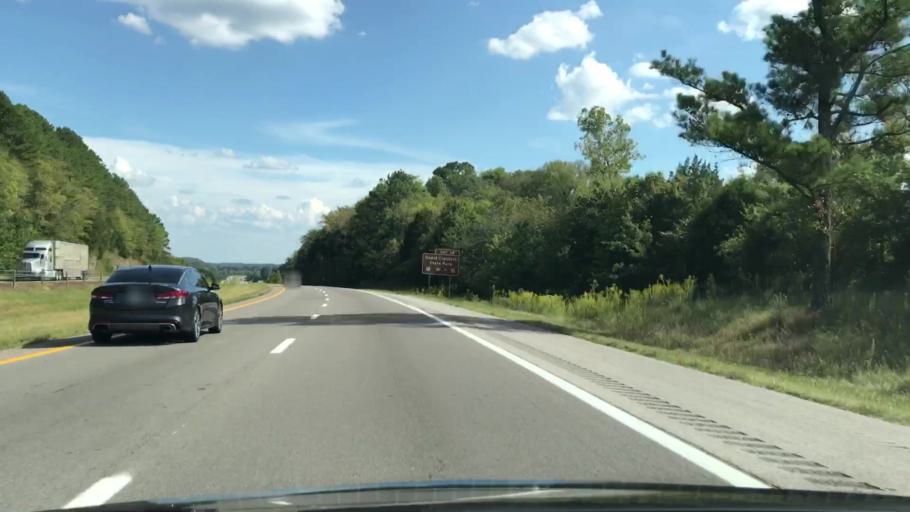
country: US
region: Tennessee
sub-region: Giles County
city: Pulaski
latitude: 35.2190
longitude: -86.8883
